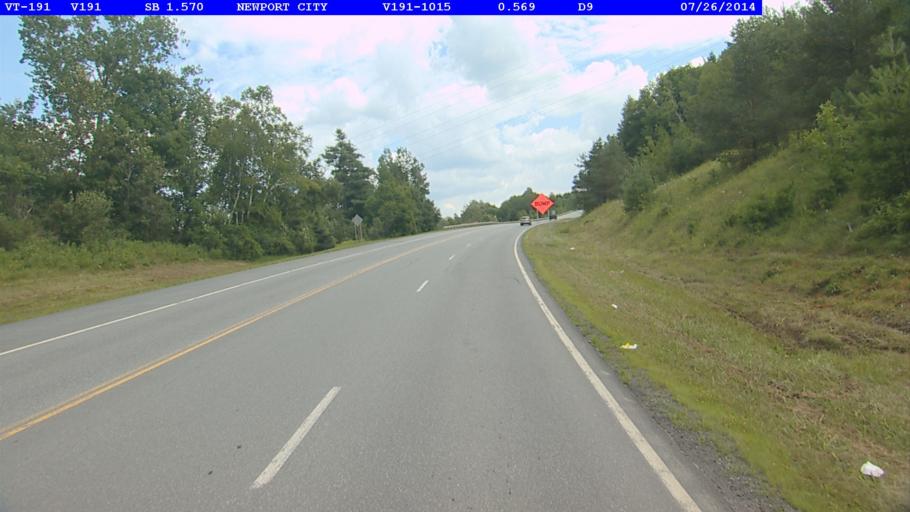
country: US
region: Vermont
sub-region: Orleans County
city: Newport
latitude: 44.9375
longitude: -72.1909
